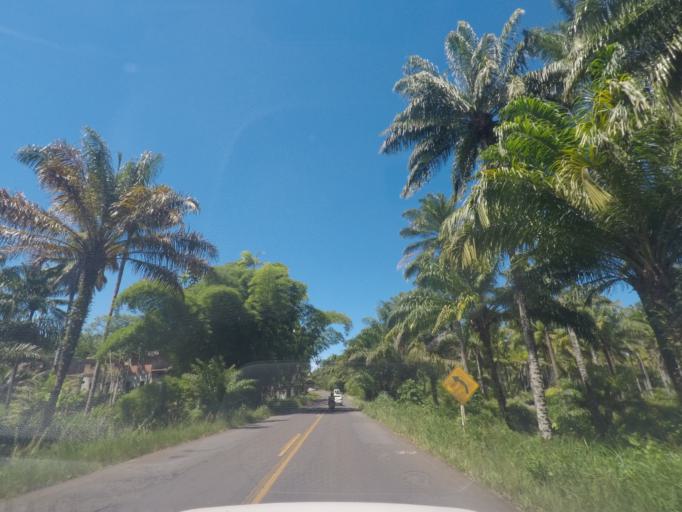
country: BR
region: Bahia
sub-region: Taperoa
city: Taperoa
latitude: -13.4690
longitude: -39.0881
